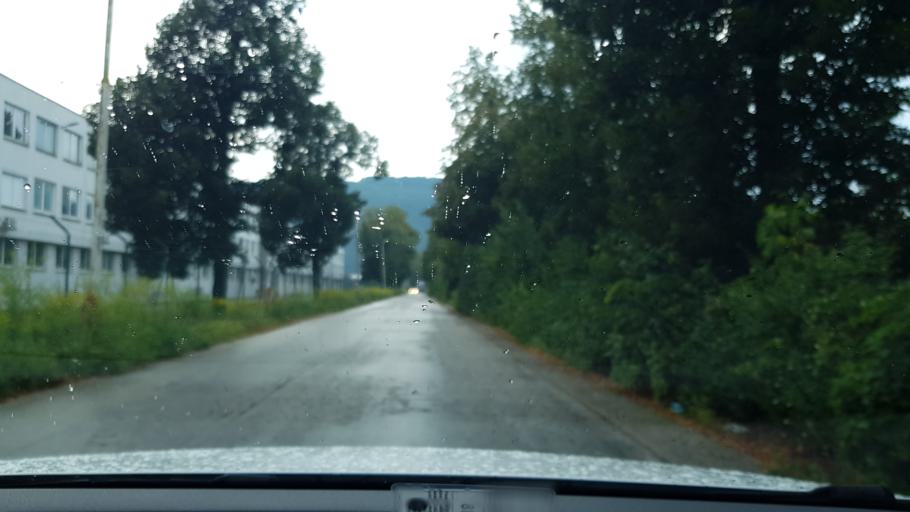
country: SK
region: Trenciansky
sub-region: Okres Povazska Bystrica
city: Povazska Bystrica
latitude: 49.1240
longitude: 18.4267
